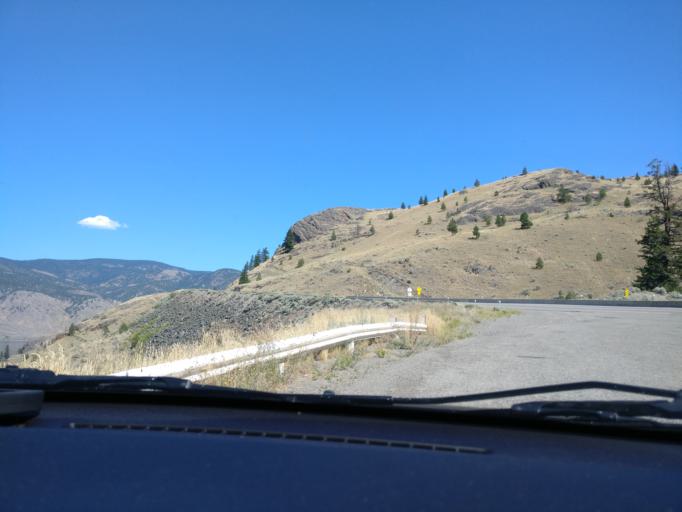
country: CA
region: British Columbia
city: Logan Lake
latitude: 50.7654
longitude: -120.7684
